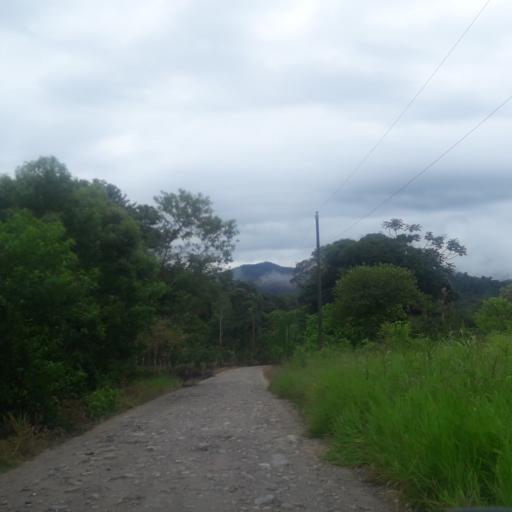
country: EC
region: Napo
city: Archidona
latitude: -0.9136
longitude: -77.8223
